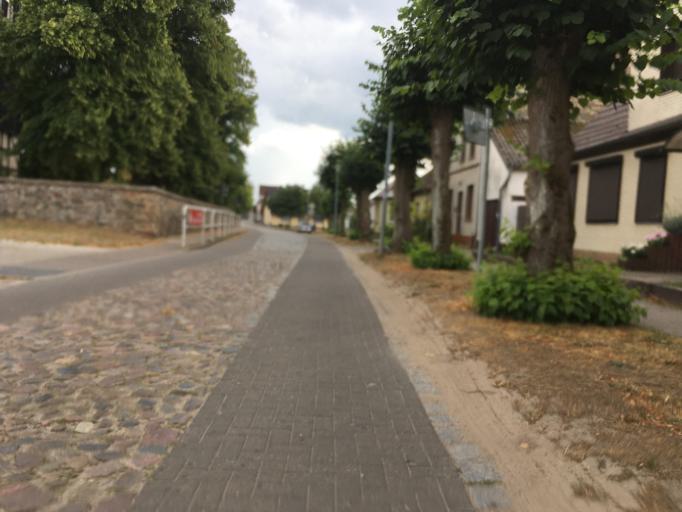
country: DE
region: Brandenburg
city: Lychen
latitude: 53.1388
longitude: 13.2420
